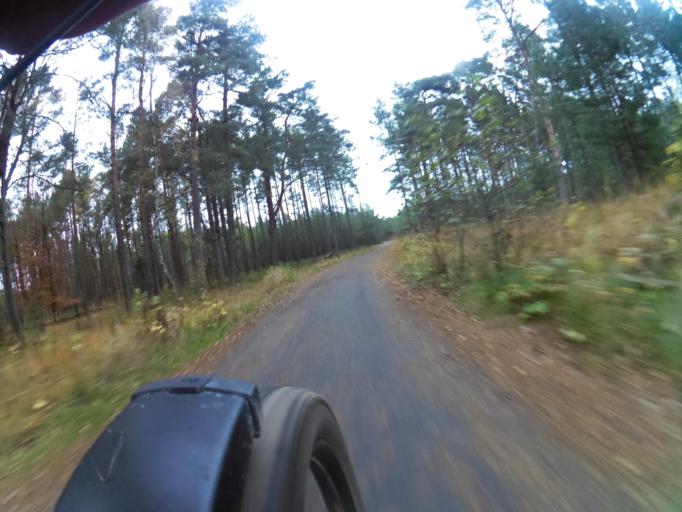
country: PL
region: Pomeranian Voivodeship
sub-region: Powiat wejherowski
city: Choczewo
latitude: 54.7862
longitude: 17.7468
